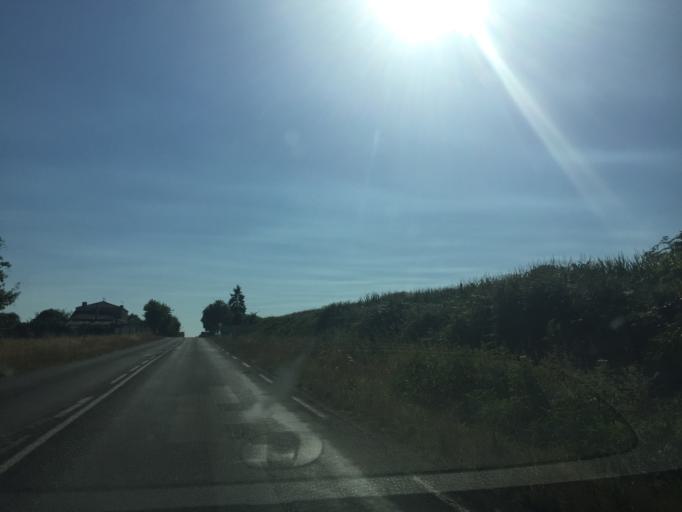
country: FR
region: Poitou-Charentes
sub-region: Departement des Deux-Sevres
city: Melle
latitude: 46.2307
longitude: -0.1207
